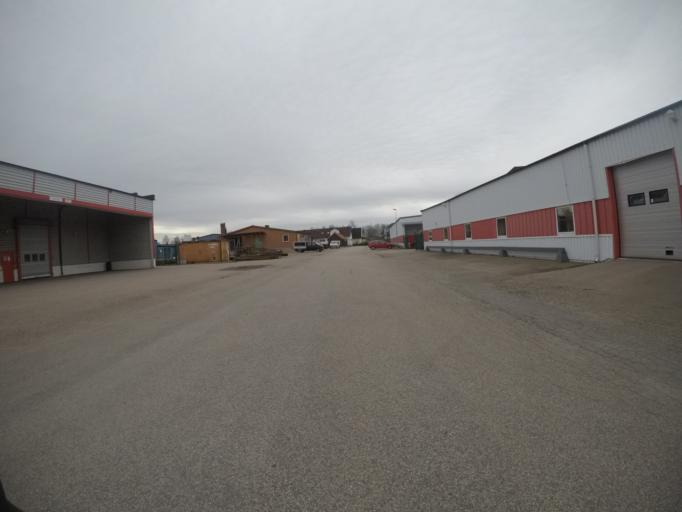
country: SE
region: Halland
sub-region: Laholms Kommun
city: Laholm
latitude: 56.5107
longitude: 13.0518
